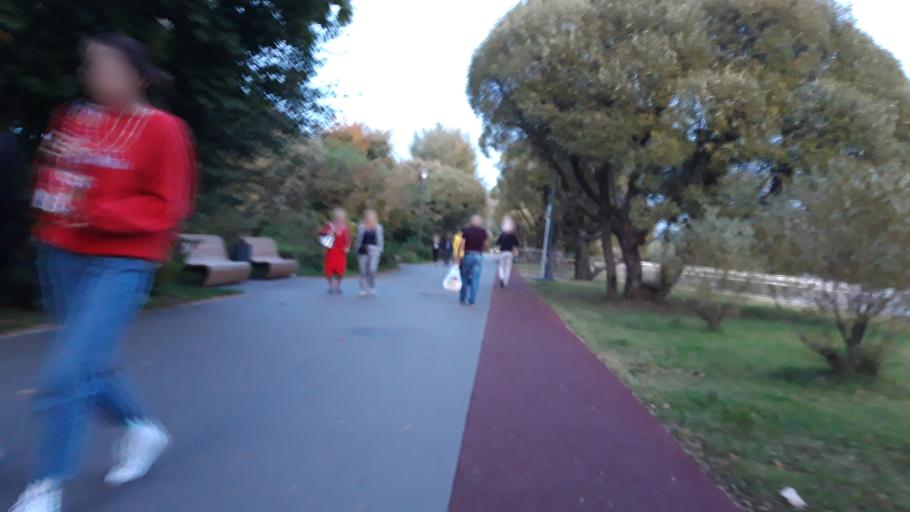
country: RU
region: Moscow
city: Zelenograd
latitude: 55.9881
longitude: 37.2139
